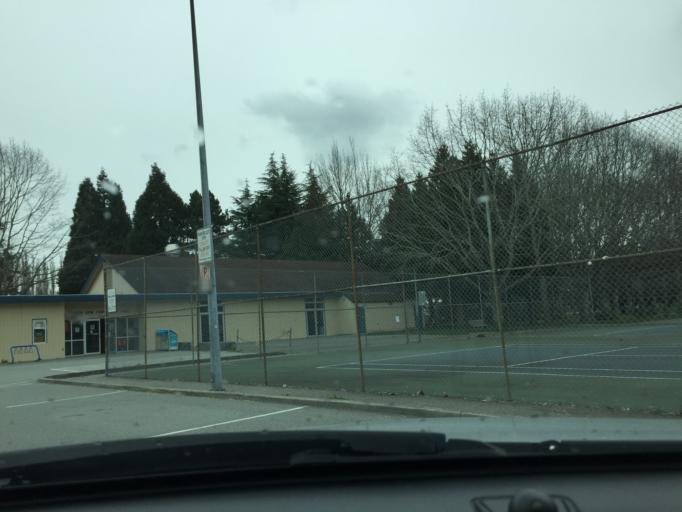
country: CA
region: British Columbia
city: Richmond
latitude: 49.1397
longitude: -123.1250
